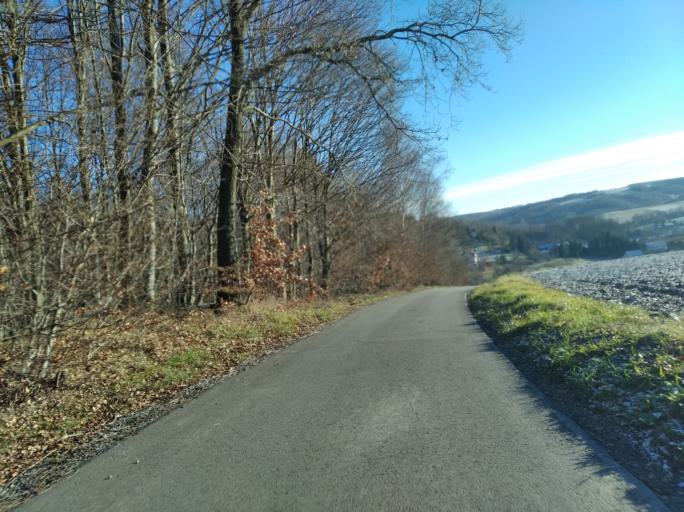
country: PL
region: Subcarpathian Voivodeship
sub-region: Powiat strzyzowski
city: Strzyzow
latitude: 49.9338
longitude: 21.7693
